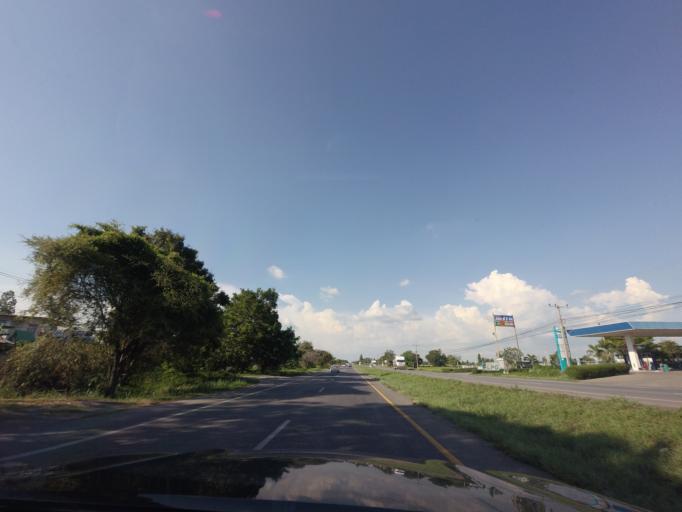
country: TH
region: Khon Kaen
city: Non Sila
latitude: 15.9994
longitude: 102.7014
